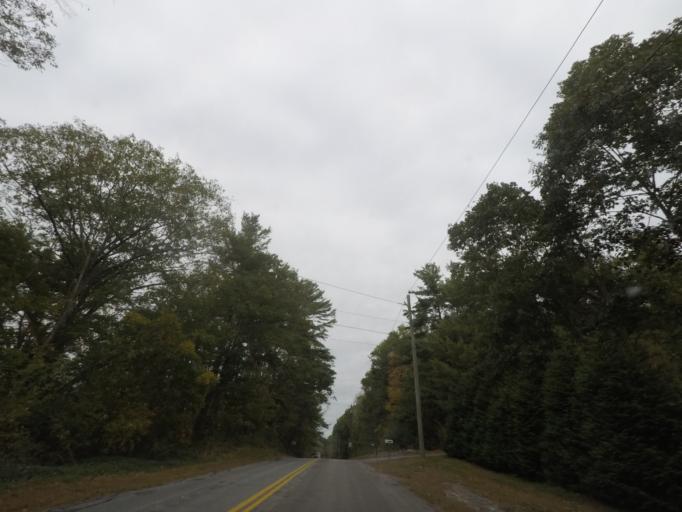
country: US
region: Connecticut
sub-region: Windham County
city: Thompson
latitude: 41.9429
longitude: -71.8330
